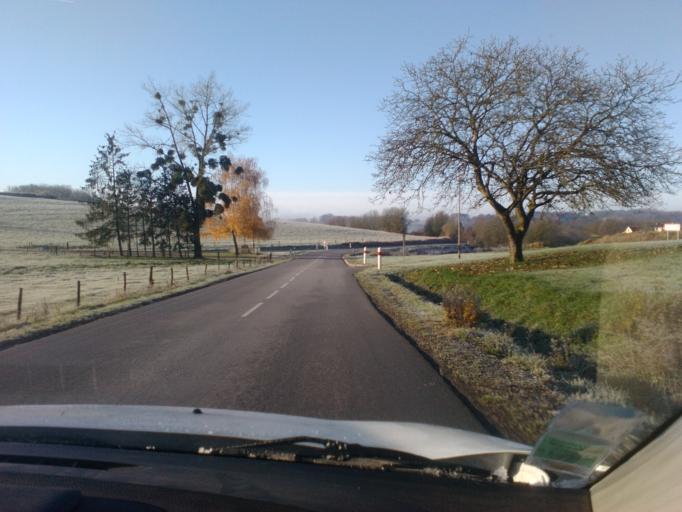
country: FR
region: Lorraine
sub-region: Departement des Vosges
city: Darnieulles
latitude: 48.1851
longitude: 6.2176
